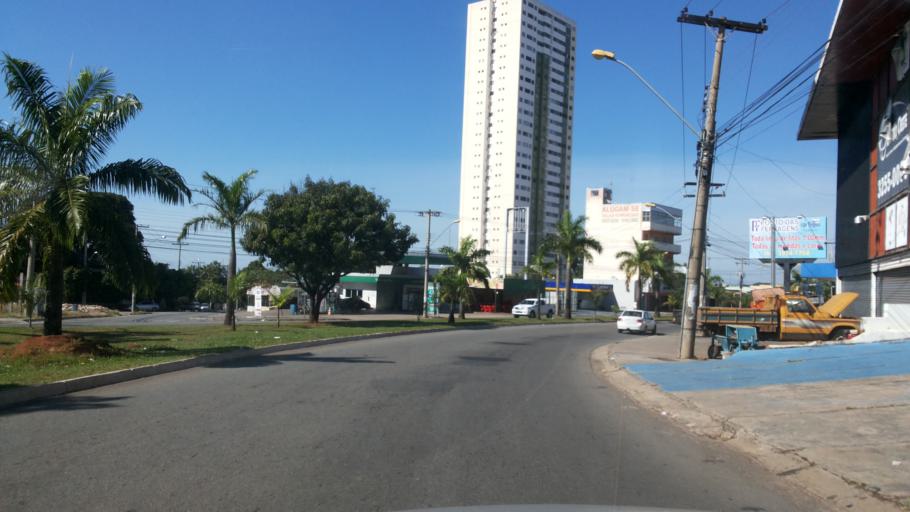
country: BR
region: Goias
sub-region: Goiania
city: Goiania
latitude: -16.7219
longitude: -49.2603
